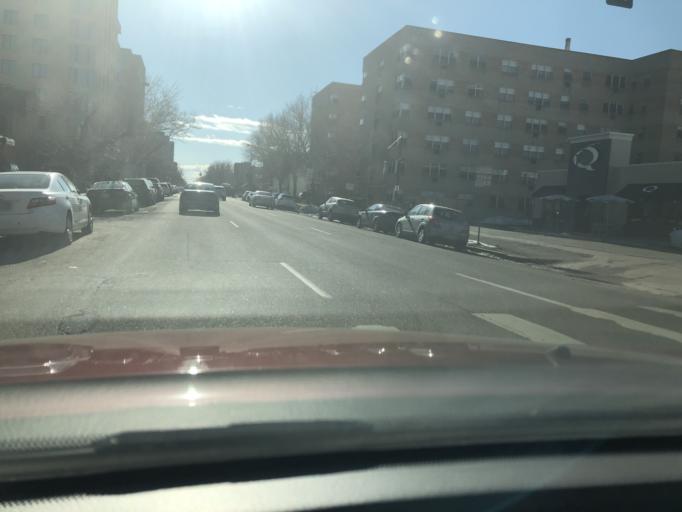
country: US
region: Colorado
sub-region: Denver County
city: Denver
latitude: 39.7368
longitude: -104.9836
